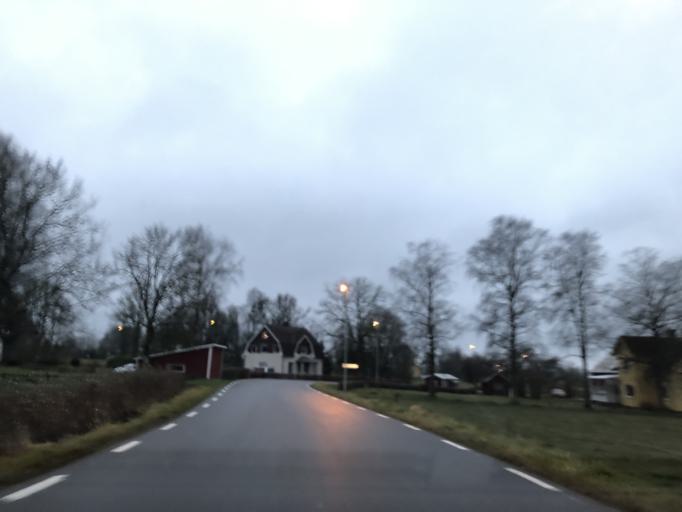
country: SE
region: Vaestra Goetaland
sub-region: Ulricehamns Kommun
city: Ulricehamn
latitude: 57.8474
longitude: 13.2378
